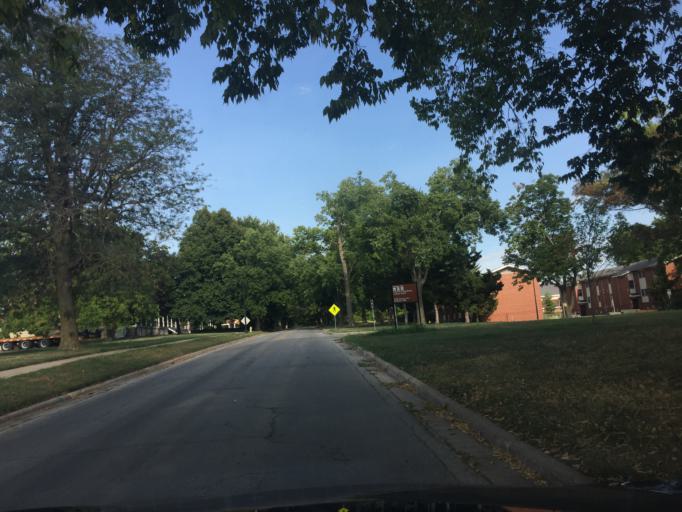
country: US
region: Kansas
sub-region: Leavenworth County
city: Leavenworth
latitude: 39.3560
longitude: -94.9252
